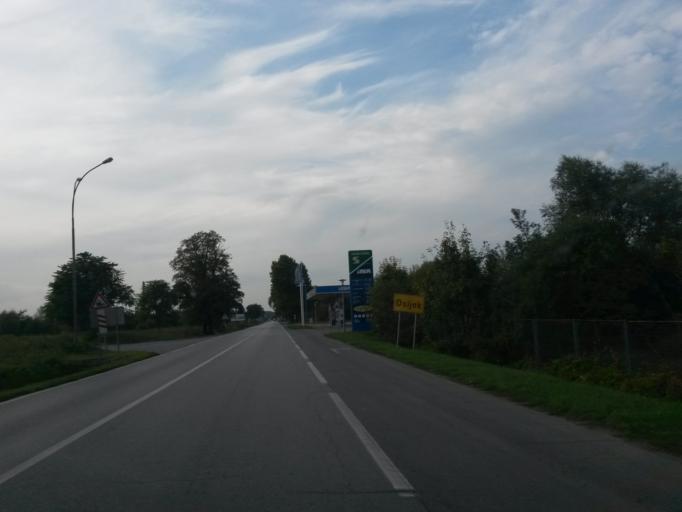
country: HR
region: Osjecko-Baranjska
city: Tenja
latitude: 45.5394
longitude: 18.7654
